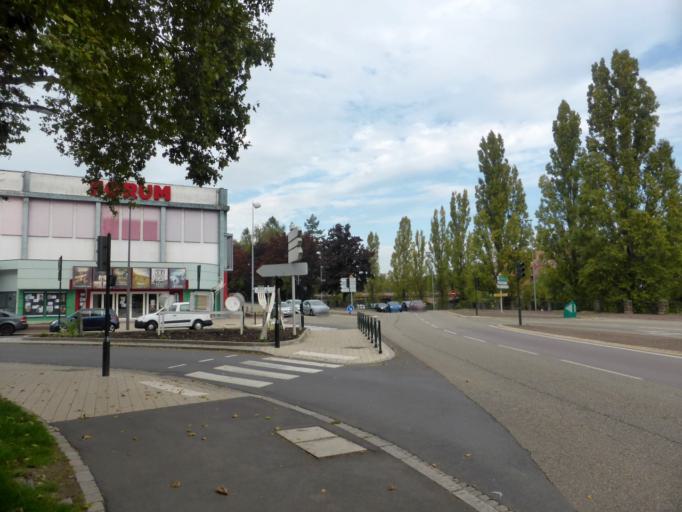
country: FR
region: Lorraine
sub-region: Departement de la Moselle
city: Sarreguemines
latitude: 49.1103
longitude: 7.0717
